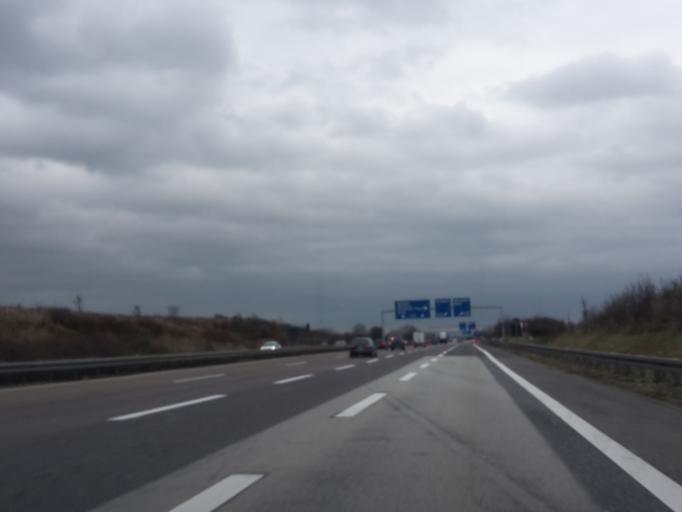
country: DE
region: Hesse
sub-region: Regierungsbezirk Darmstadt
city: Hochheim am Main
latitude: 50.0619
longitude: 8.3823
